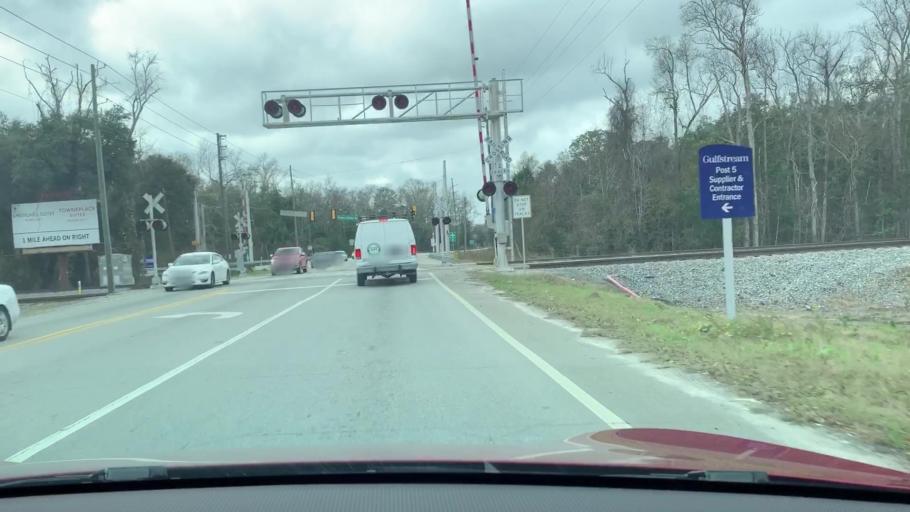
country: US
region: Georgia
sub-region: Chatham County
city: Port Wentworth
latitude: 32.1425
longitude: -81.1911
